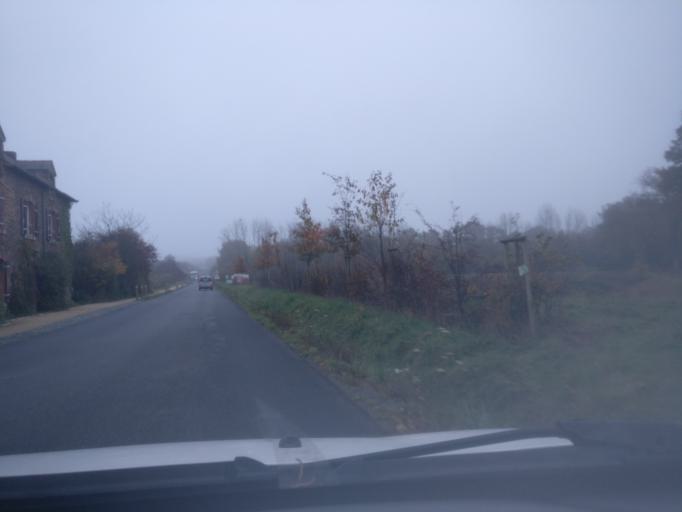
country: FR
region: Brittany
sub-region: Departement d'Ille-et-Vilaine
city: Orgeres
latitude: 48.0087
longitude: -1.6971
